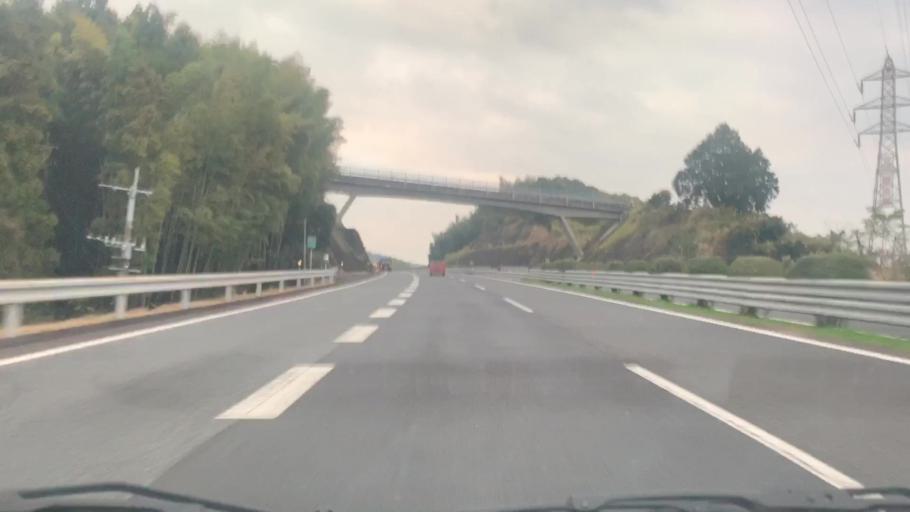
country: JP
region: Nagasaki
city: Omura
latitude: 32.9945
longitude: 129.9526
